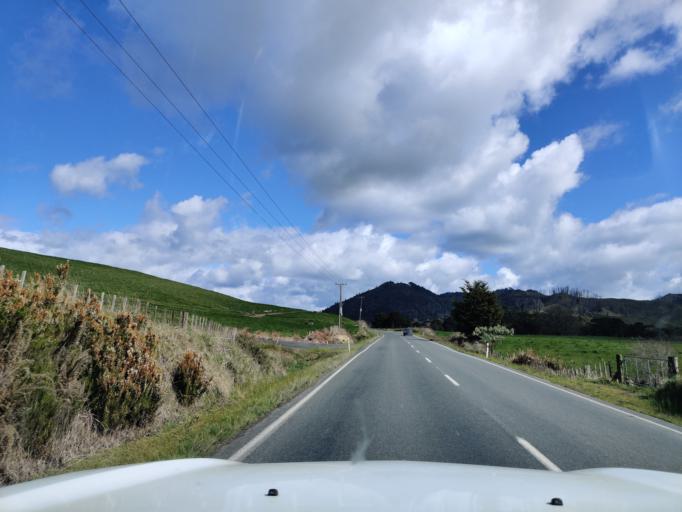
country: NZ
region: Waikato
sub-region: Waikato District
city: Ngaruawahia
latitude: -37.5892
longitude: 175.2131
